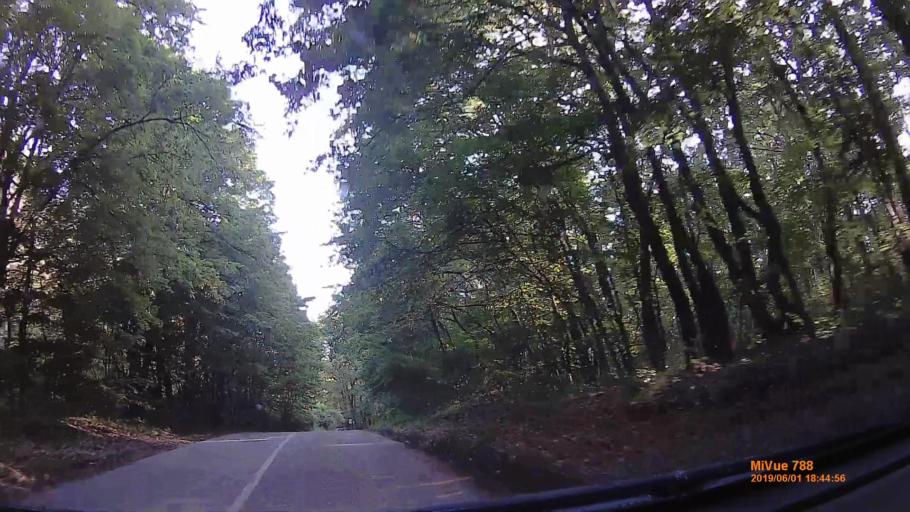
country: HU
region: Pest
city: Pilisszanto
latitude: 47.6869
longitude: 18.8869
